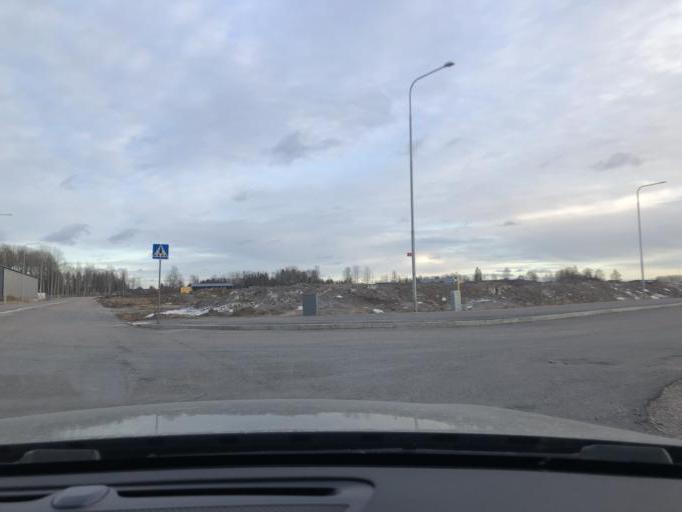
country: SE
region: Uppsala
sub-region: Tierps Kommun
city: Tierp
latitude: 60.3522
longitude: 17.4896
